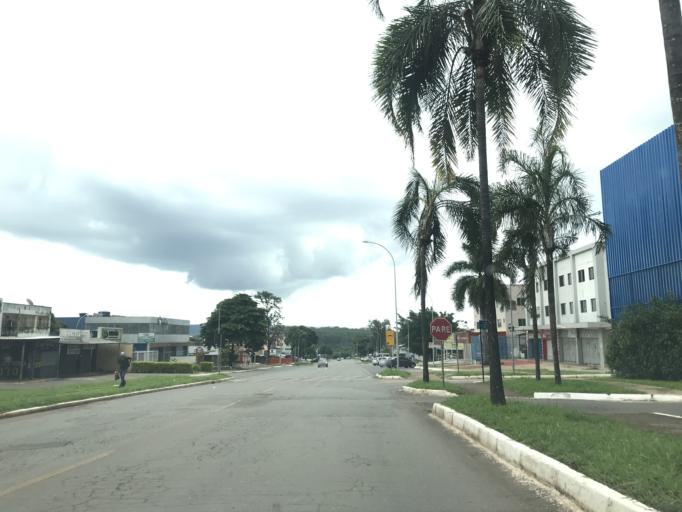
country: BR
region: Federal District
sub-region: Brasilia
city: Brasilia
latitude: -15.6429
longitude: -47.8032
